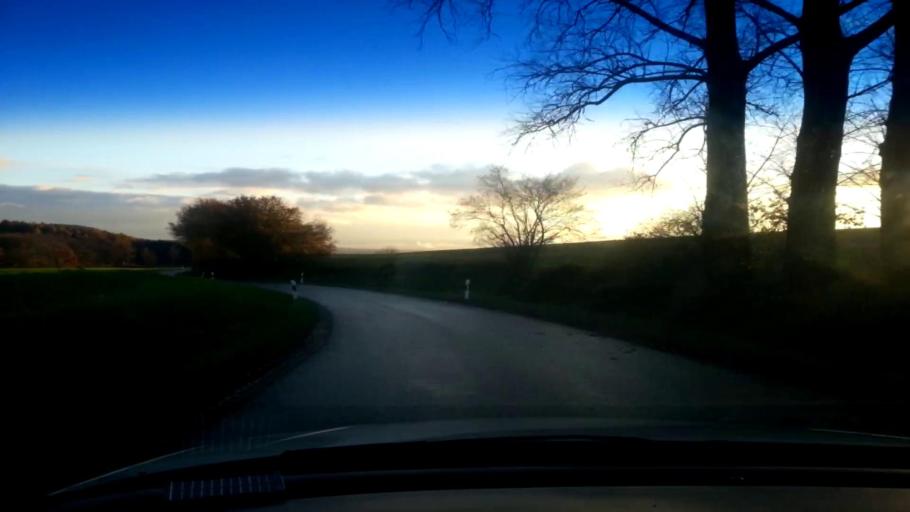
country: DE
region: Bavaria
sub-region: Upper Franconia
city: Buttenheim
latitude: 49.8250
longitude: 11.0563
